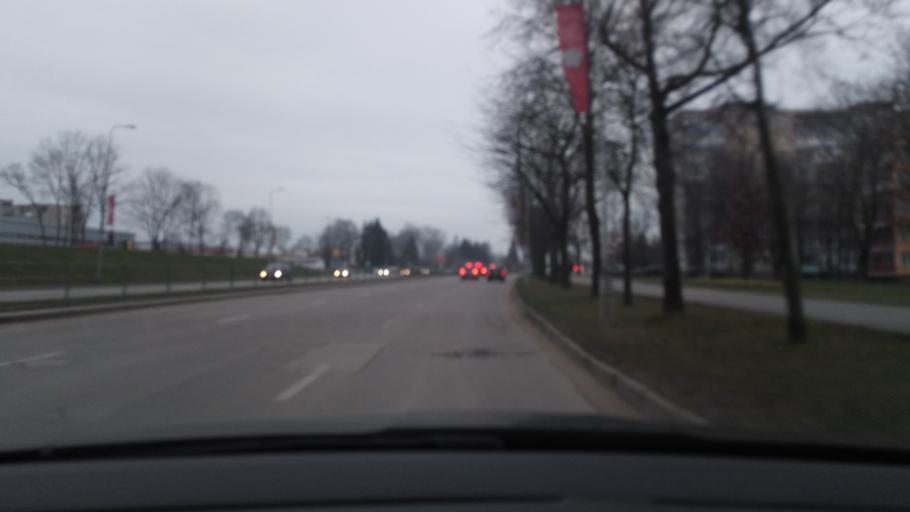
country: LT
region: Alytaus apskritis
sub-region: Alytus
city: Alytus
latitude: 54.3990
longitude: 24.0254
